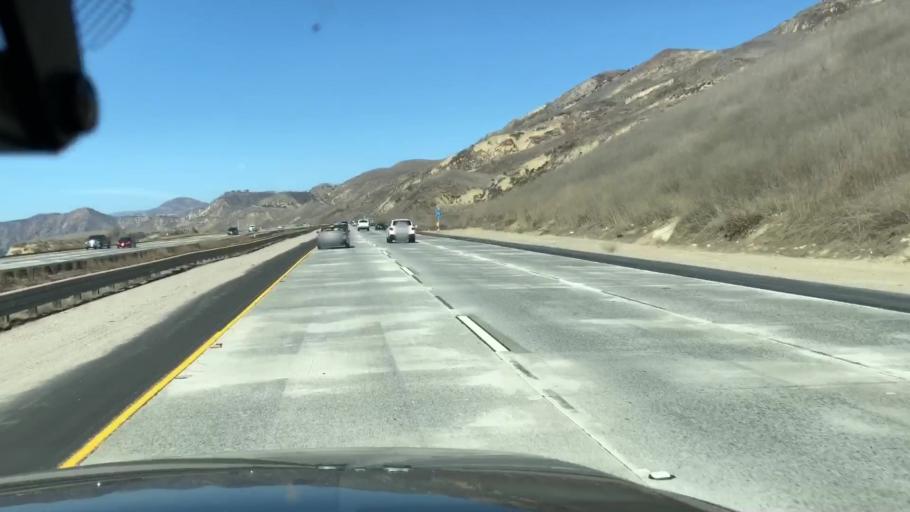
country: US
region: California
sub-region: Ventura County
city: Ventura
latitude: 34.2963
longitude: -119.3403
